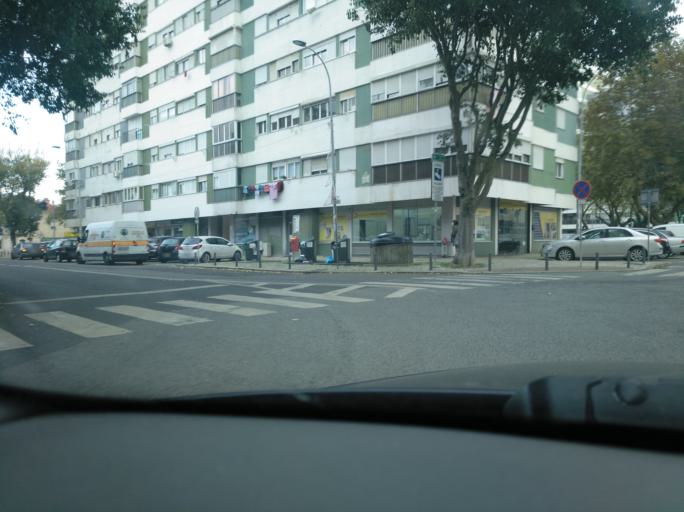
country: PT
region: Lisbon
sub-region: Amadora
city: Amadora
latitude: 38.7531
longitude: -9.2120
